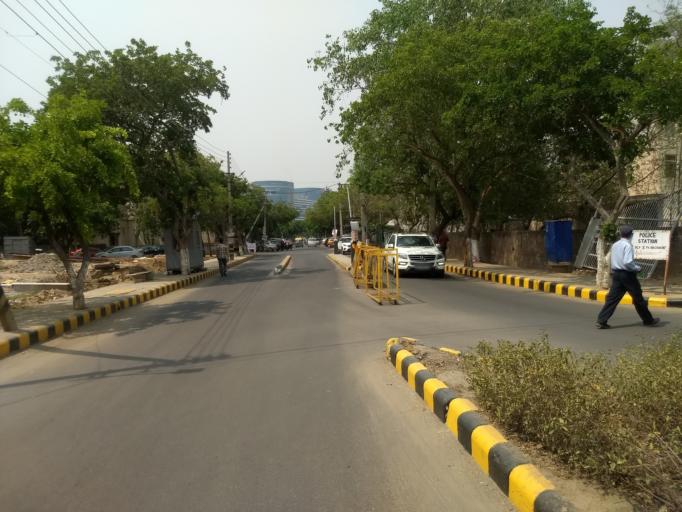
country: IN
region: Haryana
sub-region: Gurgaon
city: Gurgaon
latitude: 28.4813
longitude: 77.0916
